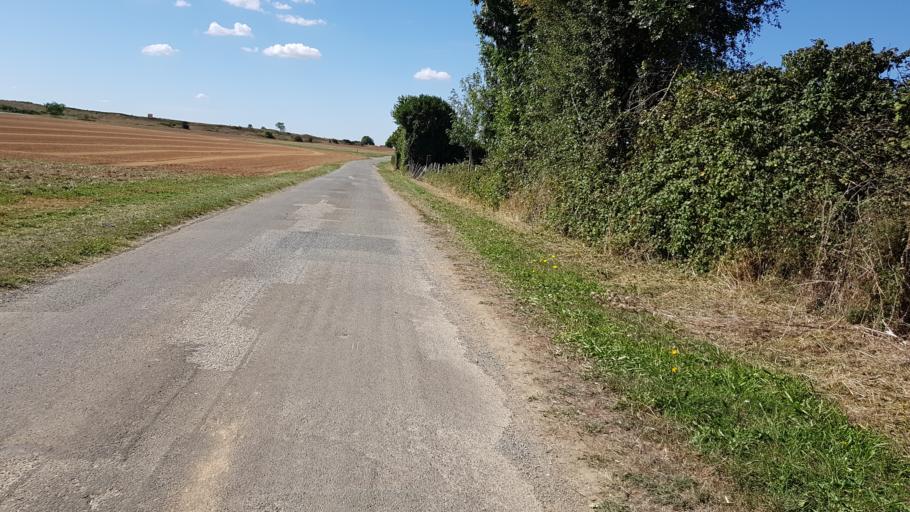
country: FR
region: Poitou-Charentes
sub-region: Departement des Deux-Sevres
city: Vouille
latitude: 46.3160
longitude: -0.3809
